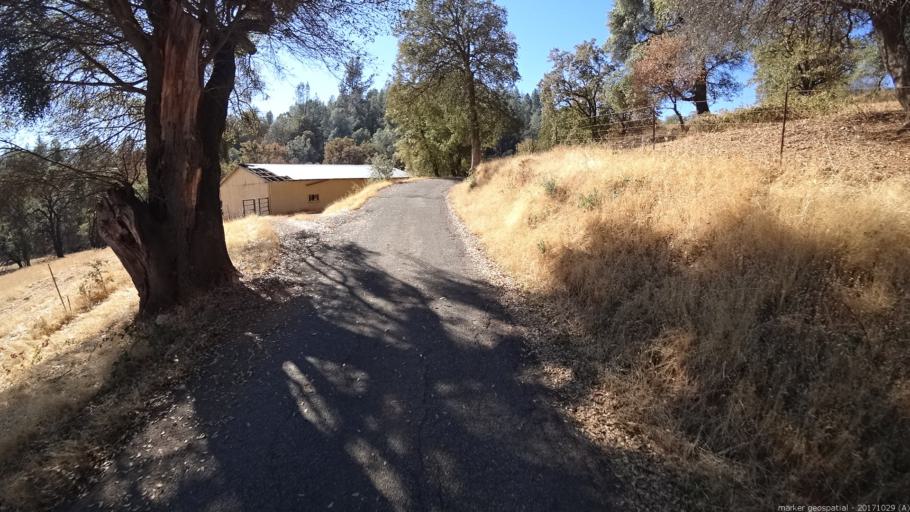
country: US
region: California
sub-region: Shasta County
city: Shasta
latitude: 40.4661
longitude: -122.6912
